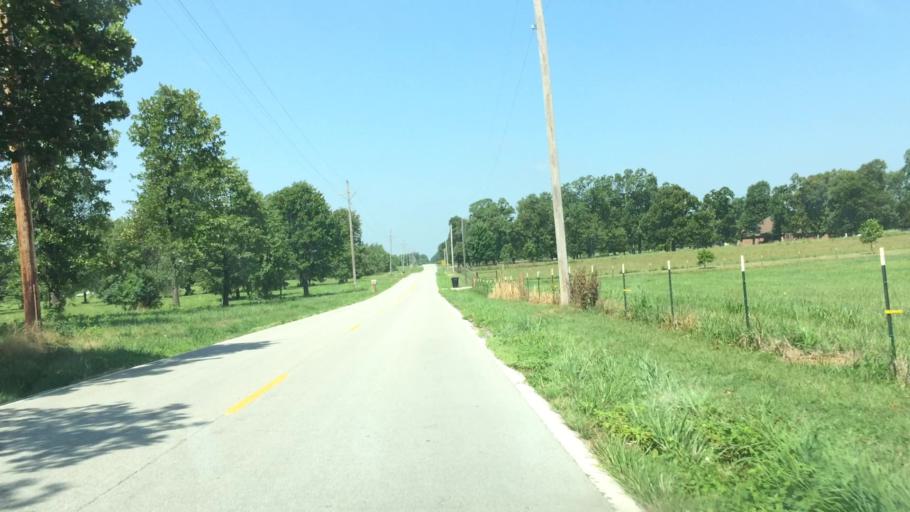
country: US
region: Missouri
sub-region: Greene County
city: Strafford
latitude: 37.2715
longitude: -93.1636
